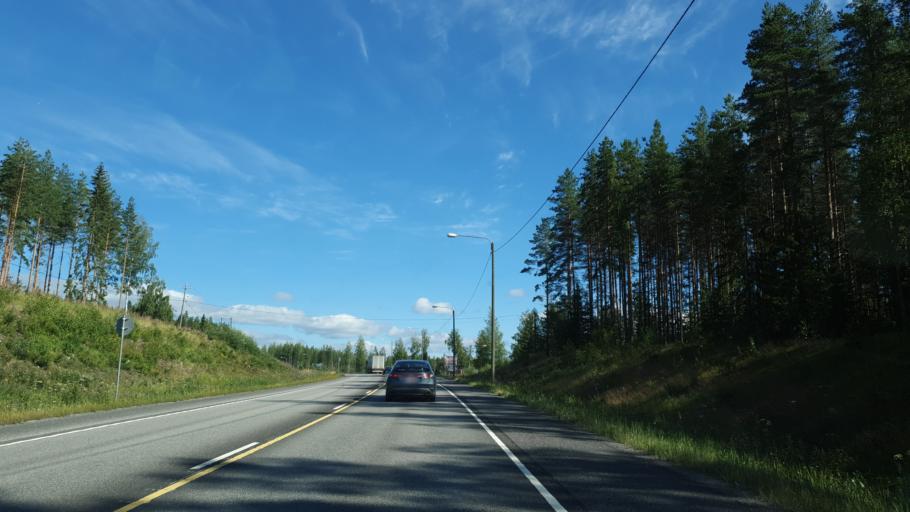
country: FI
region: Central Finland
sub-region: Jyvaeskylae
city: Toivakka
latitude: 62.2466
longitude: 26.0355
